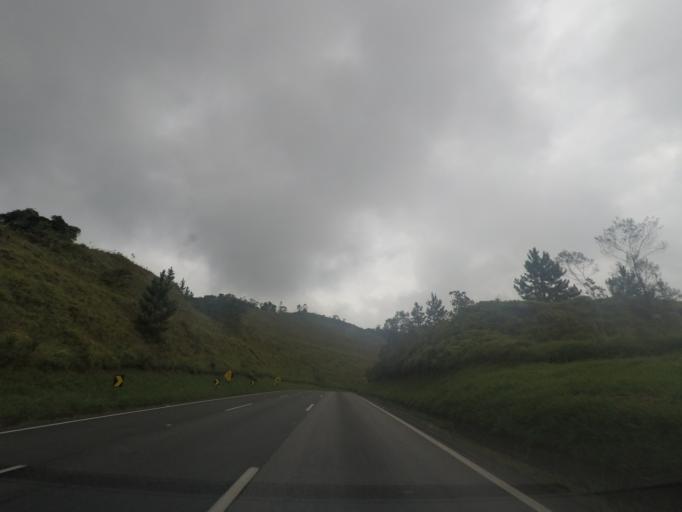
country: BR
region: Sao Paulo
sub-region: Cajati
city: Cajati
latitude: -24.9534
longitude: -48.4431
